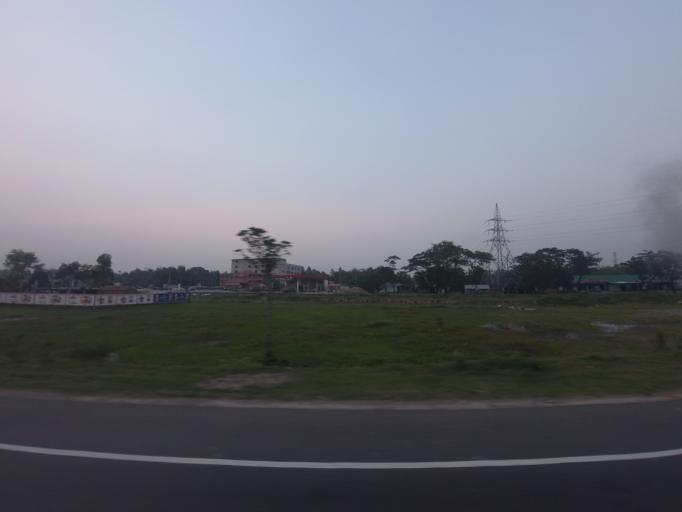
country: BD
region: Chittagong
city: Comilla
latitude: 23.4772
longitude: 91.0934
